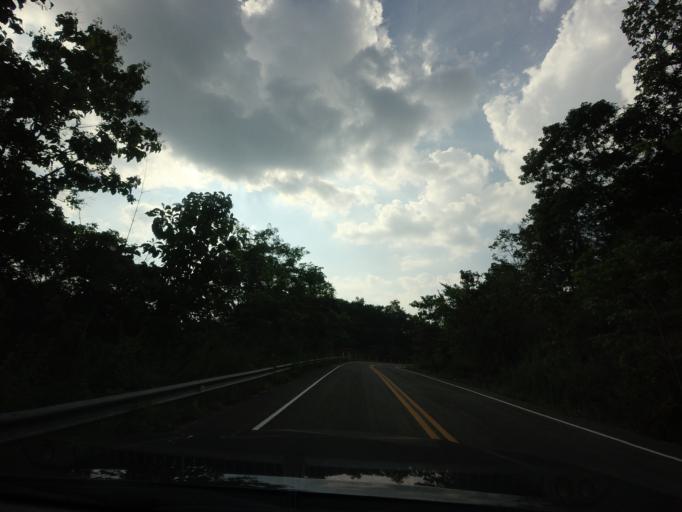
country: TH
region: Nan
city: Na Noi
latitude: 18.2892
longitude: 100.9040
